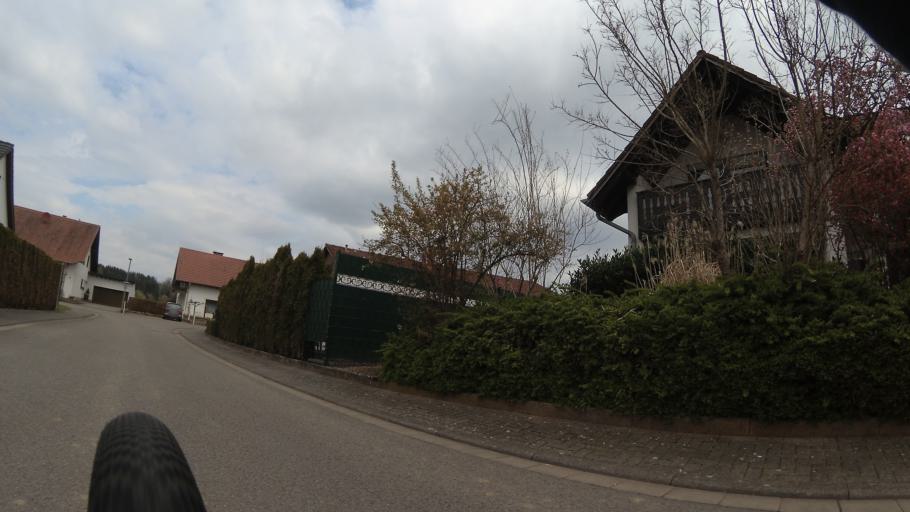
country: DE
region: Saarland
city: Mettlach
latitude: 49.4660
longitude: 6.5876
